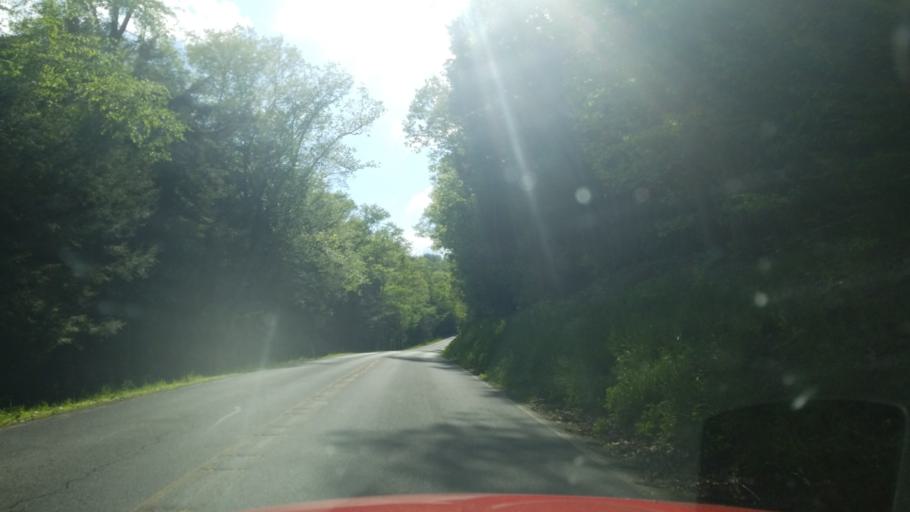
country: US
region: Pennsylvania
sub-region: Clearfield County
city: Hyde
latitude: 40.9713
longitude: -78.4261
